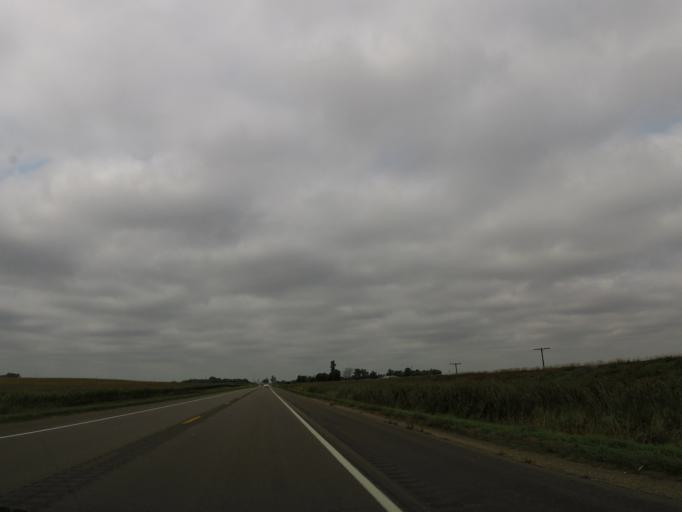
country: US
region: Minnesota
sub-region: Renville County
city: Olivia
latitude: 44.7843
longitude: -95.0464
